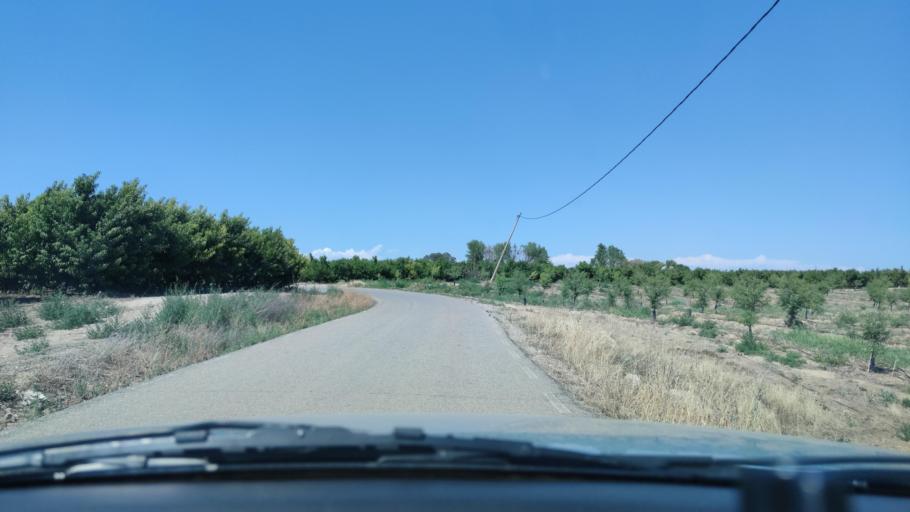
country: ES
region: Catalonia
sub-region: Provincia de Lleida
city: Torrefarrera
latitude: 41.6874
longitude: 0.6216
